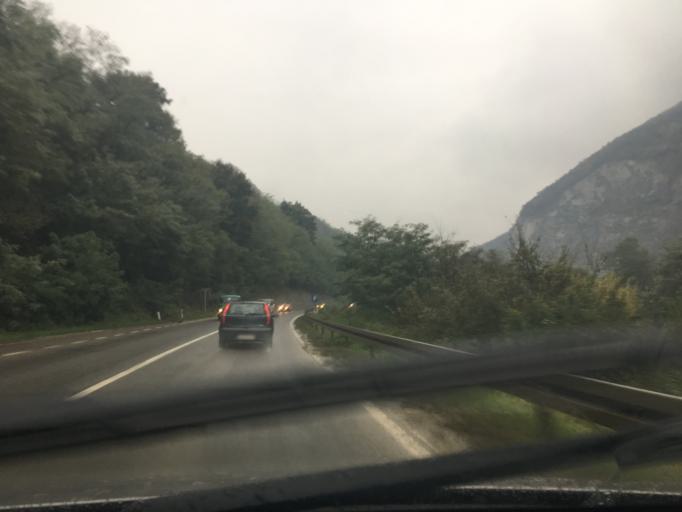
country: RS
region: Central Serbia
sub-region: Pcinjski Okrug
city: Vladicin Han
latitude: 42.7555
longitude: 22.0822
